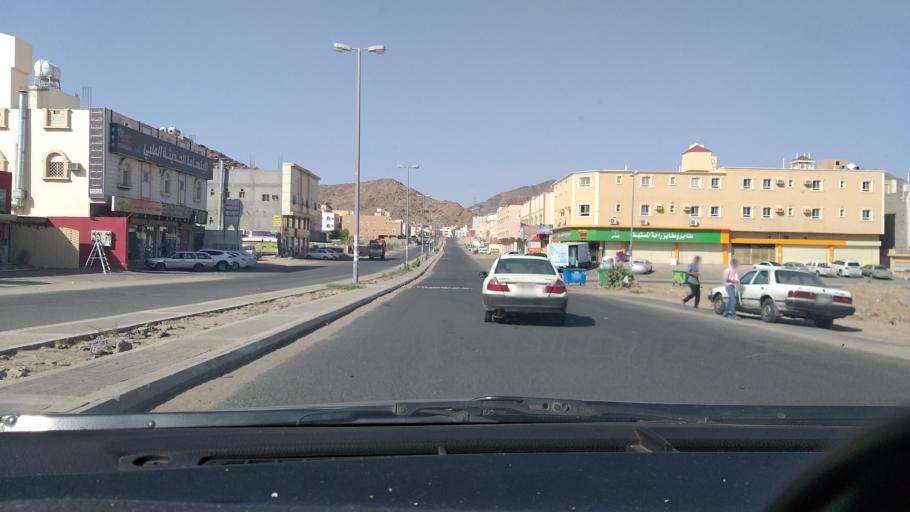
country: SA
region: Makkah
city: Ta'if
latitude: 21.2263
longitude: 40.3770
